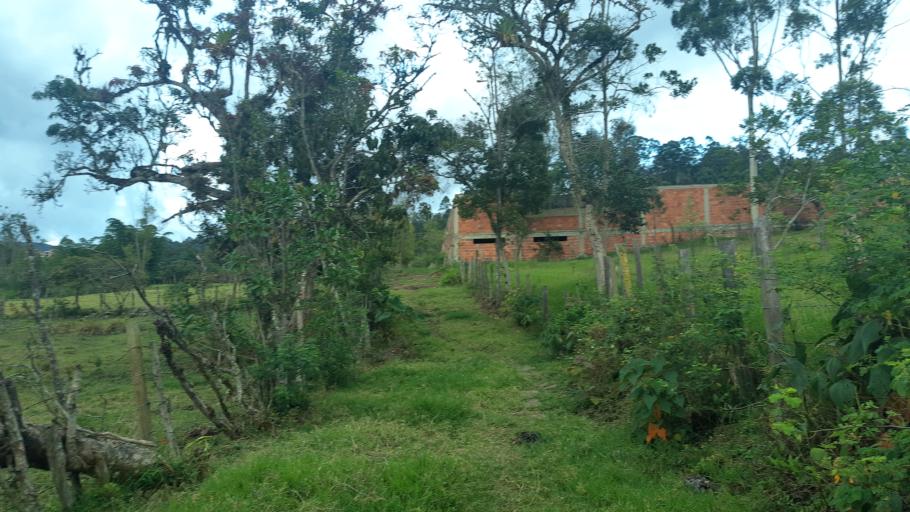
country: CO
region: Boyaca
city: Garagoa
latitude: 5.0797
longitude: -73.3758
